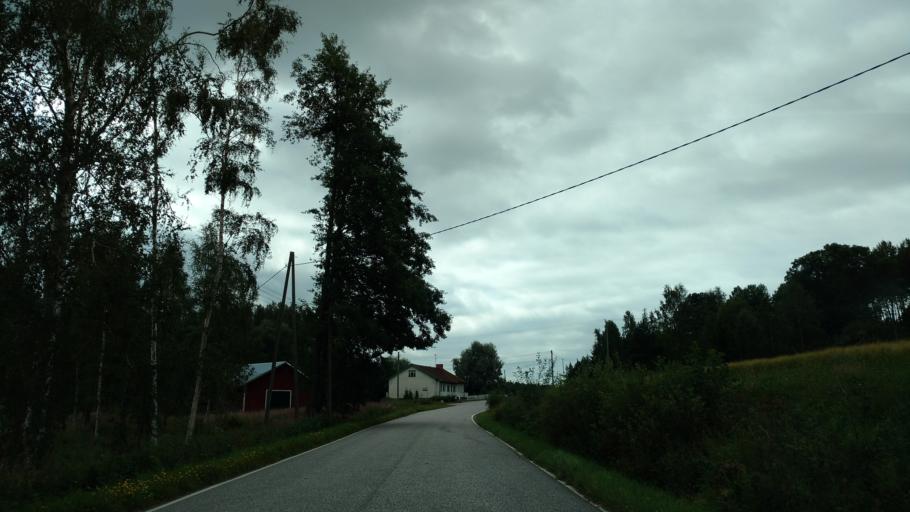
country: FI
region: Varsinais-Suomi
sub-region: Aboland-Turunmaa
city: Dragsfjaerd
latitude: 60.0506
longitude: 22.4541
